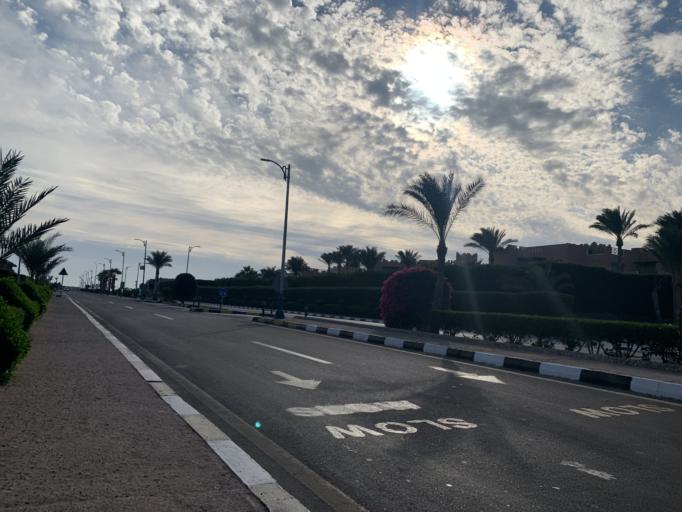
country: EG
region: South Sinai
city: Sharm el-Sheikh
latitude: 28.0192
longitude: 34.4347
